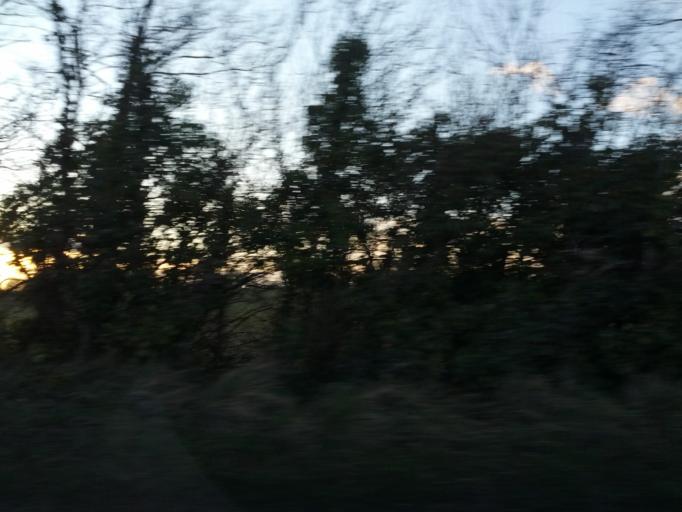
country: IE
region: Connaught
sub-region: County Galway
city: Athenry
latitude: 53.2934
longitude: -8.6319
